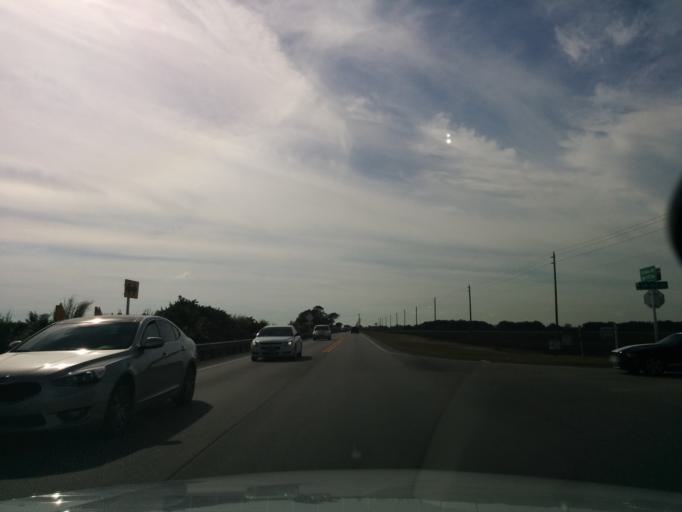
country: US
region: Florida
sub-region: Miami-Dade County
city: The Hammocks
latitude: 25.6671
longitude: -80.4811
